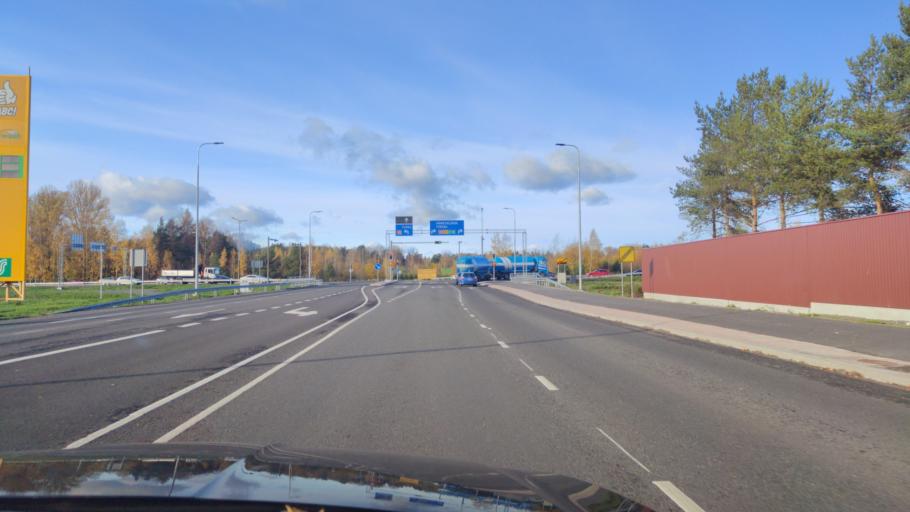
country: FI
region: Varsinais-Suomi
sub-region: Turku
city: Kaarina
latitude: 60.4660
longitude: 22.3485
